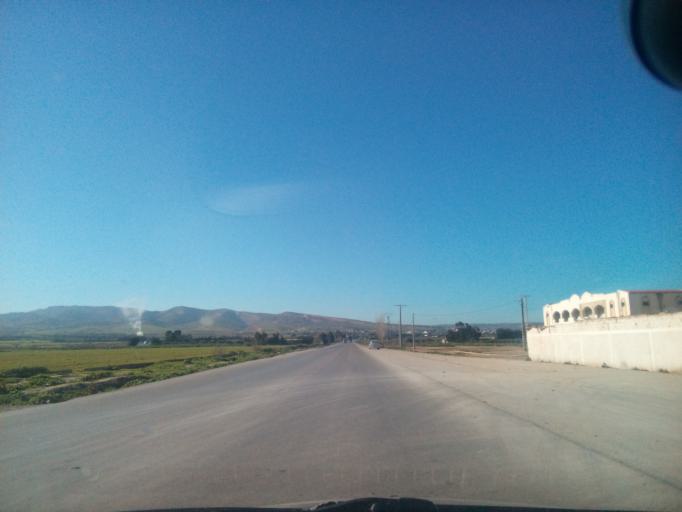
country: DZ
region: Relizane
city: Relizane
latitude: 35.8979
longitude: 0.5433
